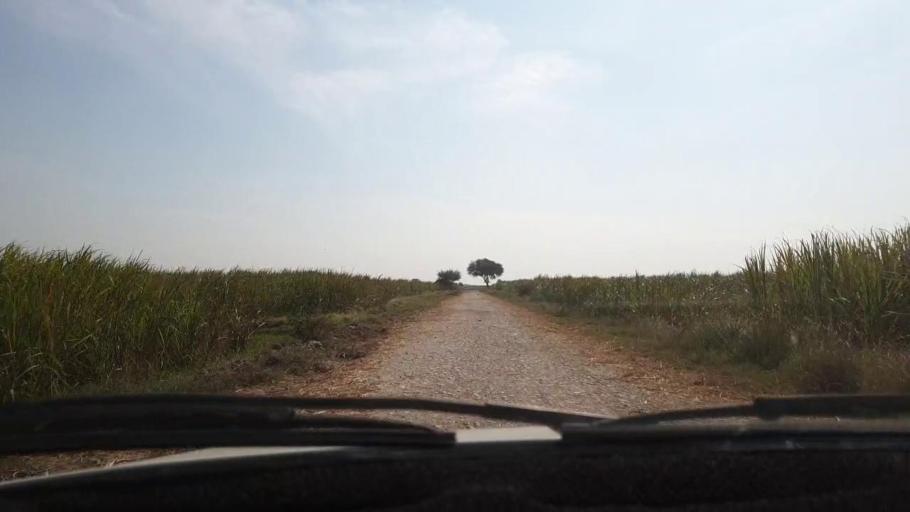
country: PK
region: Sindh
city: Bulri
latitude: 24.9545
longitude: 68.4444
